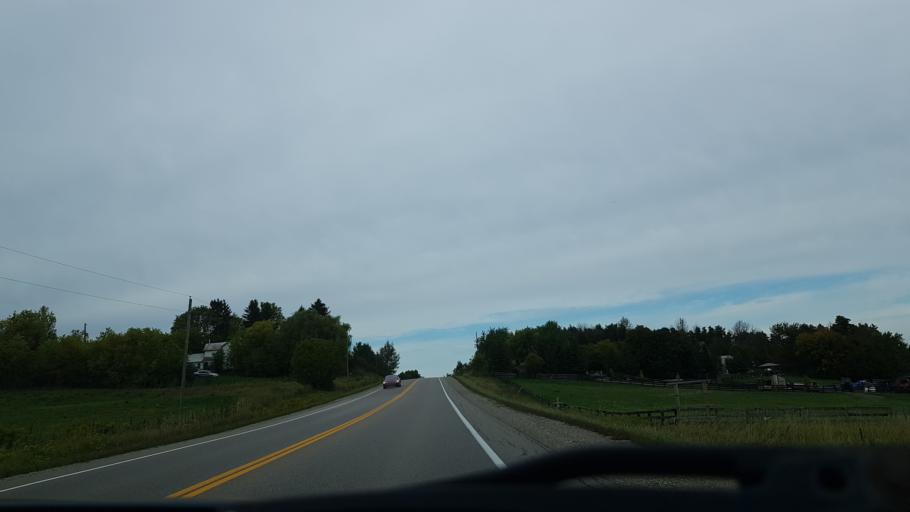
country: CA
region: Ontario
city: Orangeville
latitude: 44.0379
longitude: -80.0081
